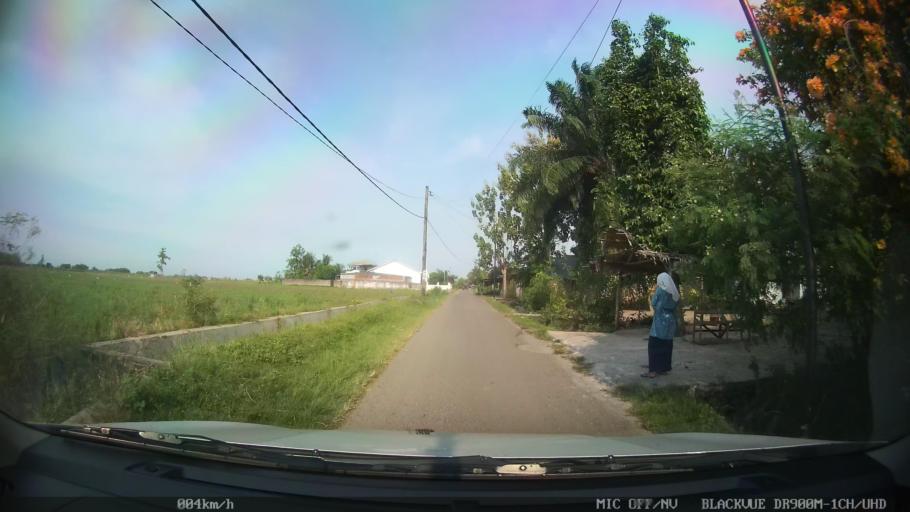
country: ID
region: North Sumatra
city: Binjai
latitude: 3.6210
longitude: 98.5236
